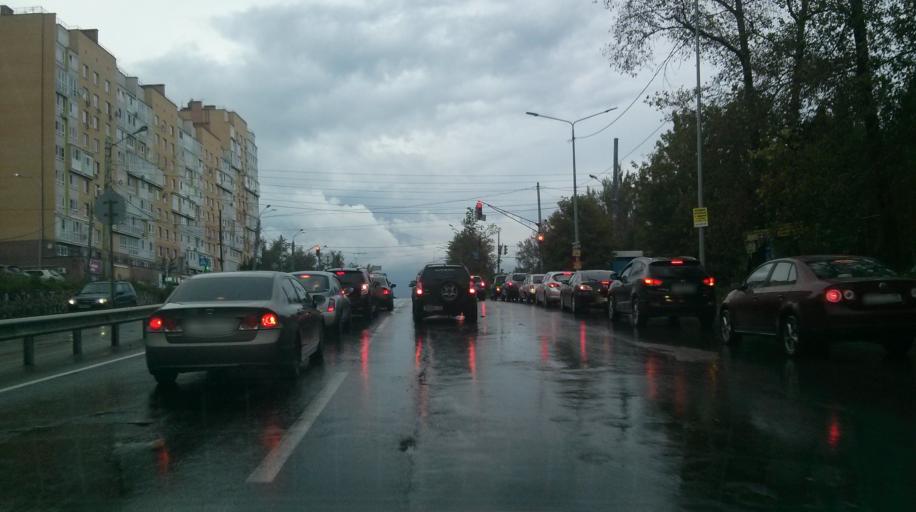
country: RU
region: Nizjnij Novgorod
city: Nizhniy Novgorod
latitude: 56.2825
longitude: 44.0364
